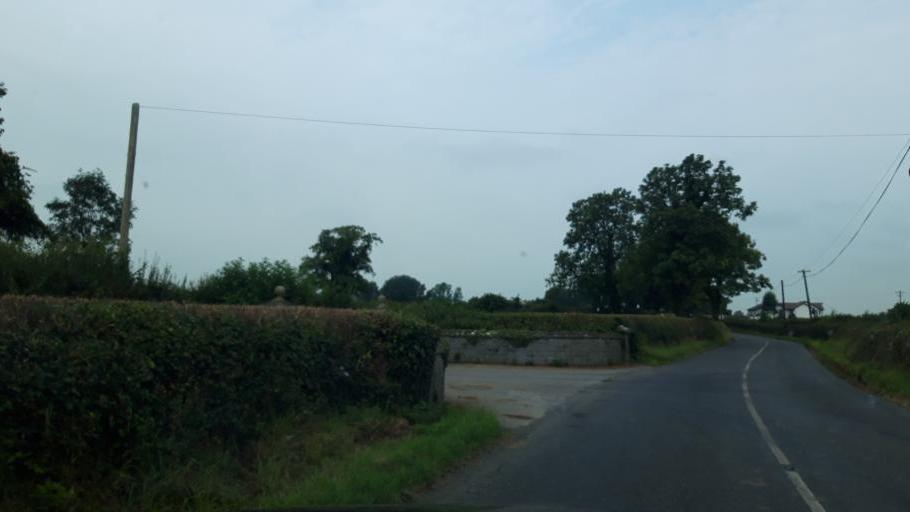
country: IE
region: Leinster
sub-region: Kilkenny
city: Callan
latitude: 52.5105
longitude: -7.4808
